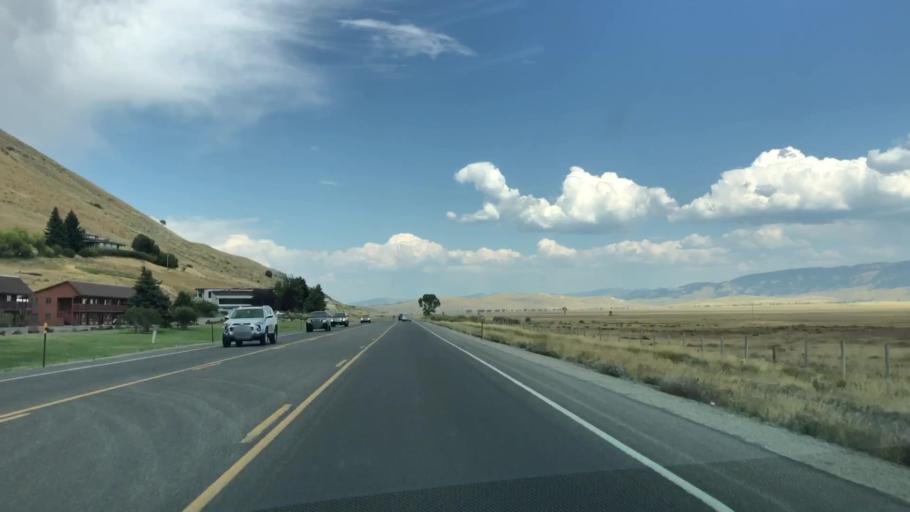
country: US
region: Wyoming
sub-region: Teton County
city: Jackson
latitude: 43.5061
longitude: -110.7585
